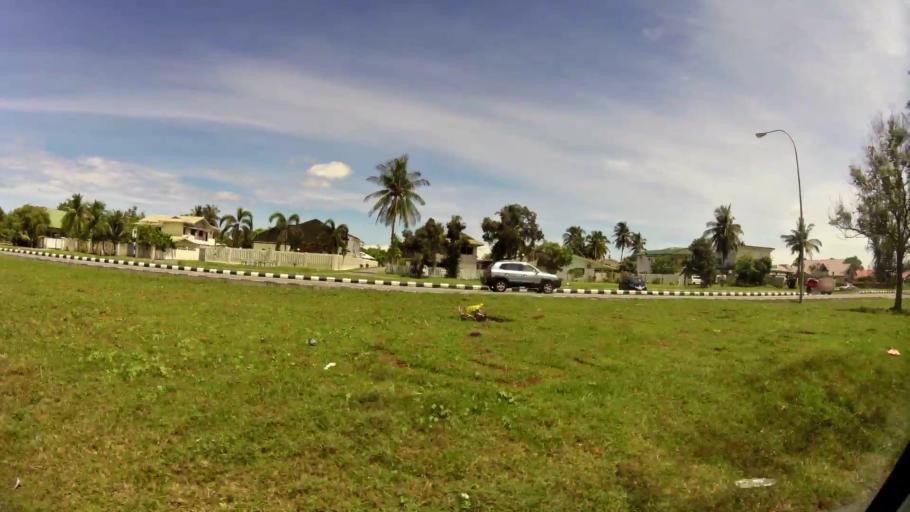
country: BN
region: Belait
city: Kuala Belait
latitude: 4.5950
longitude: 114.2434
